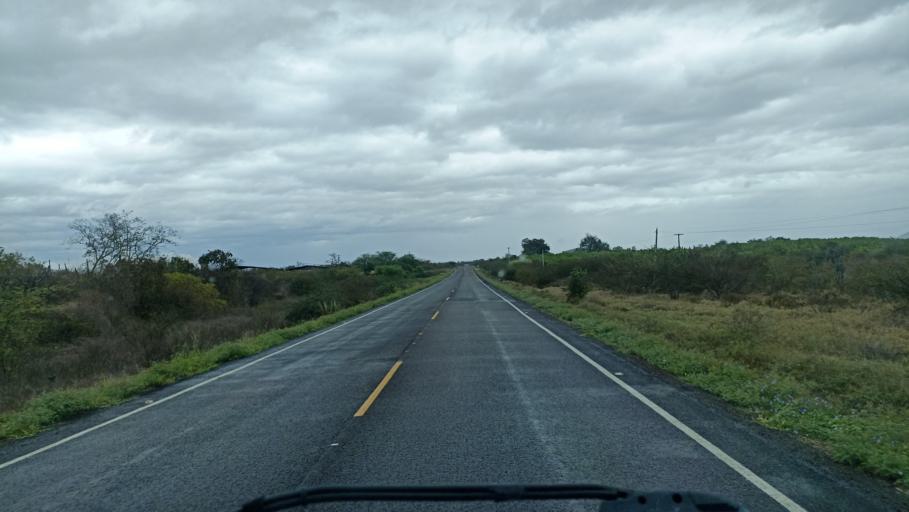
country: BR
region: Bahia
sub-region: Iacu
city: Iacu
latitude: -12.9705
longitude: -40.4997
